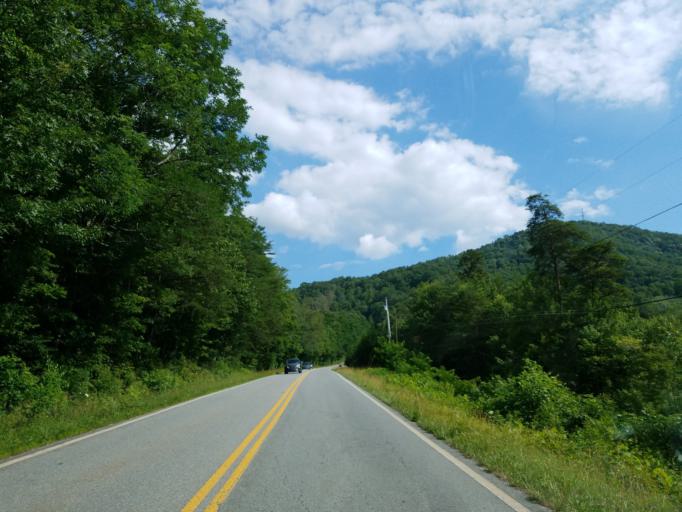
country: US
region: Georgia
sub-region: Fannin County
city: Blue Ridge
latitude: 34.8236
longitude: -84.3053
